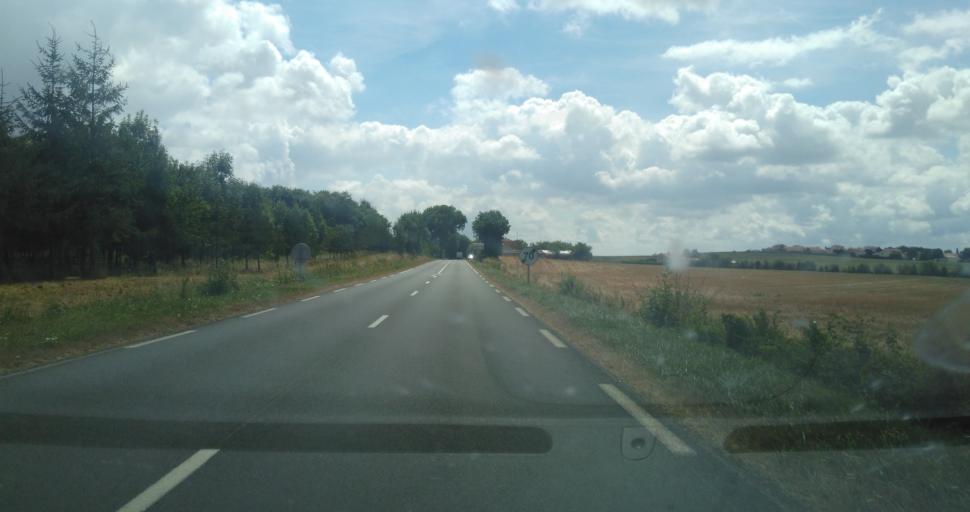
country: FR
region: Pays de la Loire
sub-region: Departement de la Vendee
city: Sainte-Hermine
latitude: 46.5661
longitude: -1.0811
